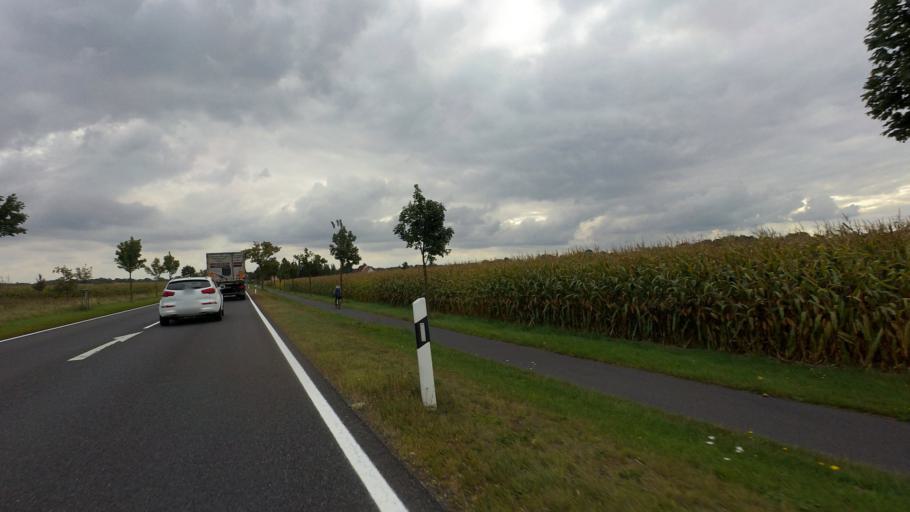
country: DE
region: Saxony
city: Neschwitz
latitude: 51.2783
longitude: 14.3378
